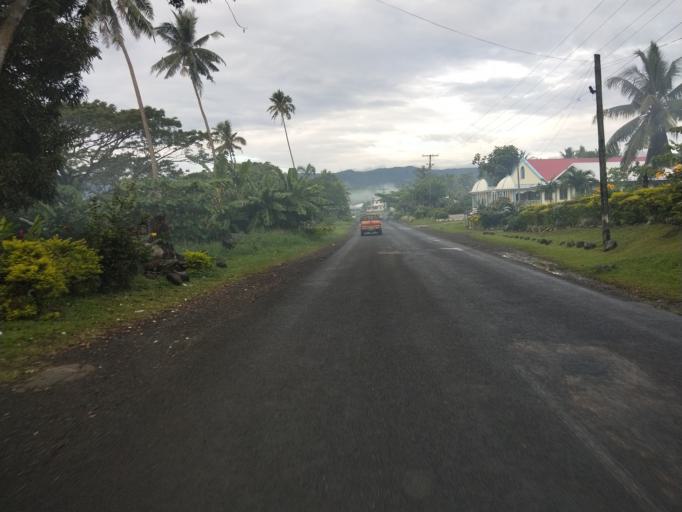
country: WS
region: Tuamasaga
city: Vaiusu
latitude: -13.8126
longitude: -171.8093
